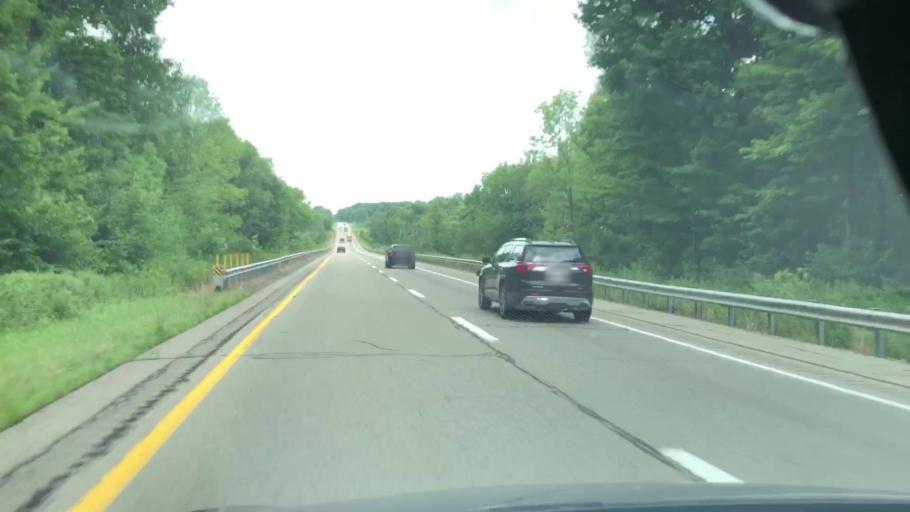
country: US
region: Pennsylvania
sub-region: Erie County
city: Edinboro
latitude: 41.8175
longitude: -80.1754
